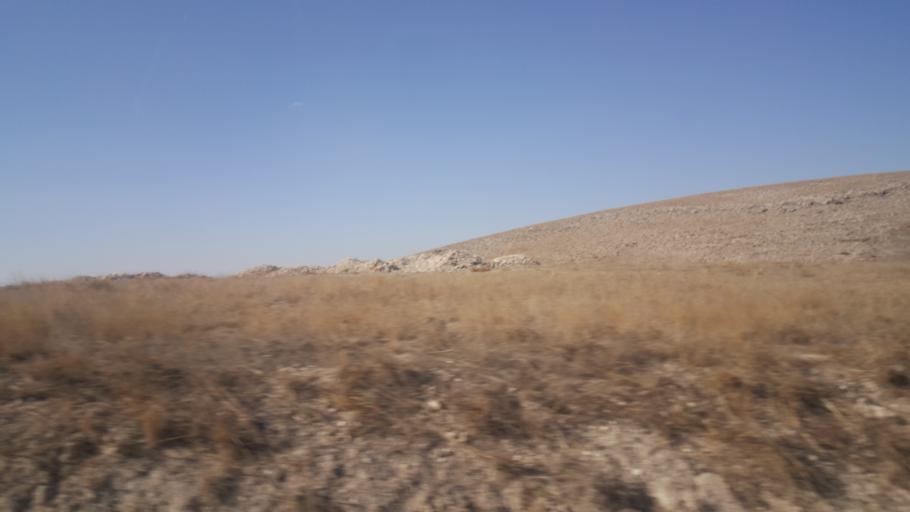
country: TR
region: Konya
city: Celtik
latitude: 39.0903
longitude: 32.0566
